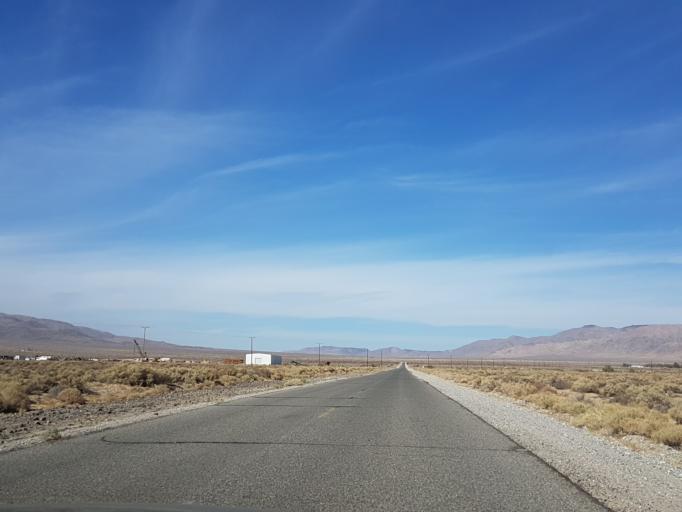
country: US
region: California
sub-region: San Bernardino County
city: Searles Valley
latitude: 35.8128
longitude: -117.3435
